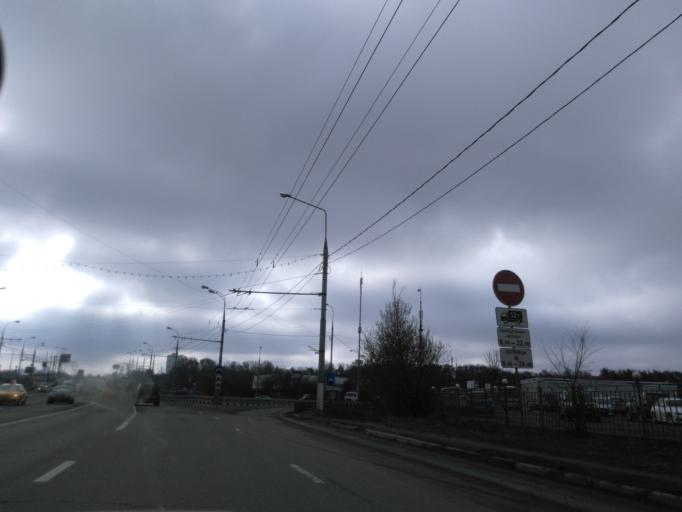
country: RU
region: Moscow
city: Khimki
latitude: 55.8782
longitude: 37.4234
